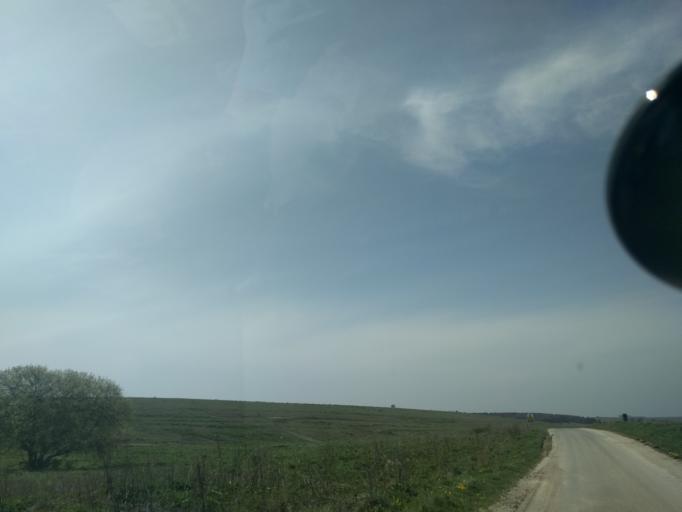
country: GB
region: England
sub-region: Wiltshire
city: Edington
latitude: 51.2366
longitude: -2.0745
